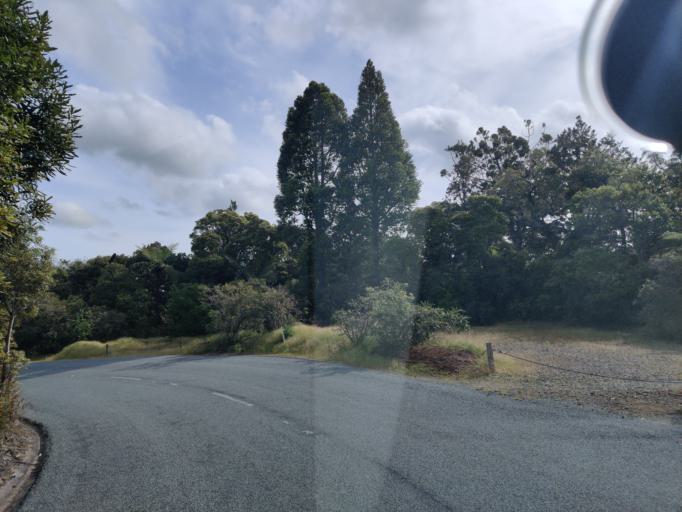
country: NZ
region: Northland
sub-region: Kaipara District
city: Dargaville
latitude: -35.6381
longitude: 173.5590
